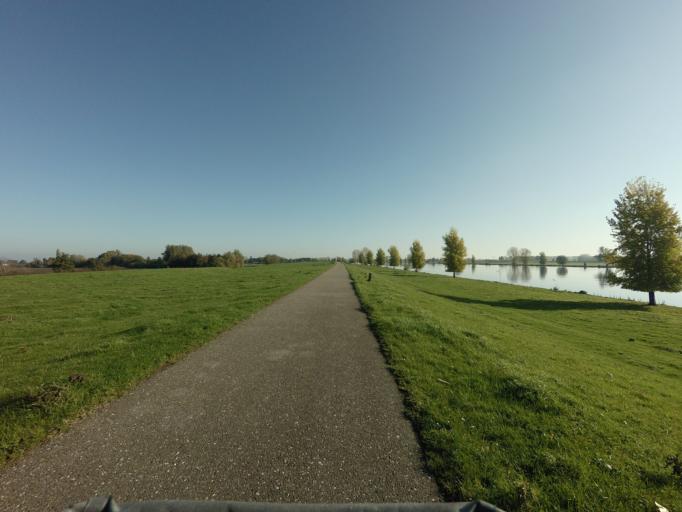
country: NL
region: North Brabant
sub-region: Gemeente Waalwijk
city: Waspik
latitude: 51.7167
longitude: 4.9957
